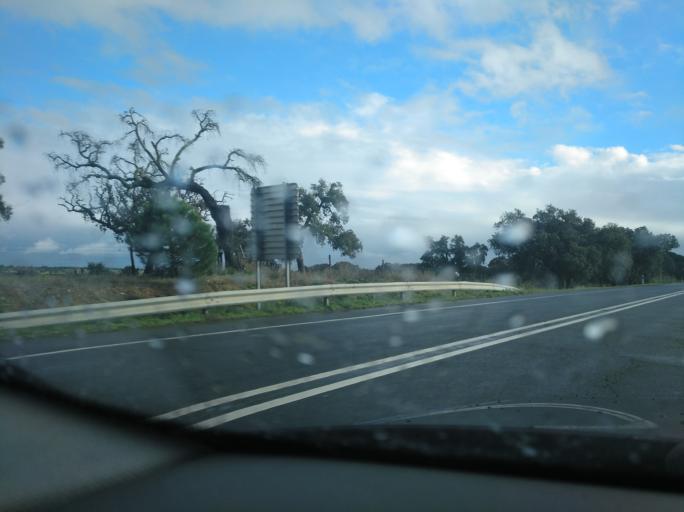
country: PT
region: Setubal
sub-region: Grandola
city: Grandola
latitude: 38.0558
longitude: -8.4038
